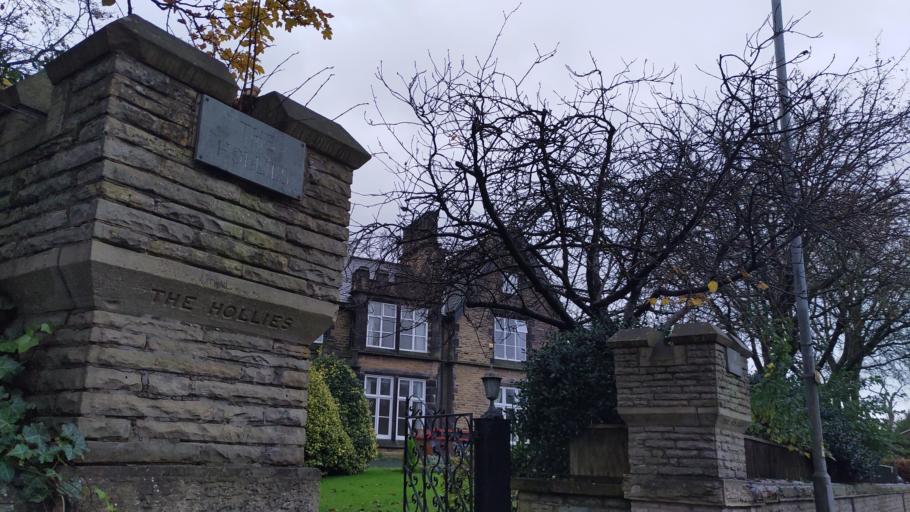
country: GB
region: England
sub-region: Borough of Rochdale
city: Rochdale
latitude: 53.6079
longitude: -2.1649
